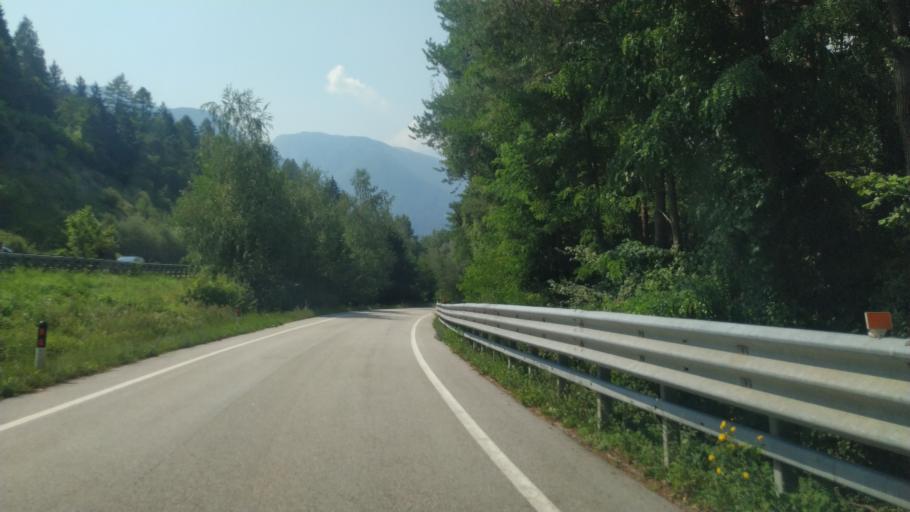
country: IT
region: Trentino-Alto Adige
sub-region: Provincia di Trento
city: Denno
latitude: 46.2773
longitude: 11.0647
